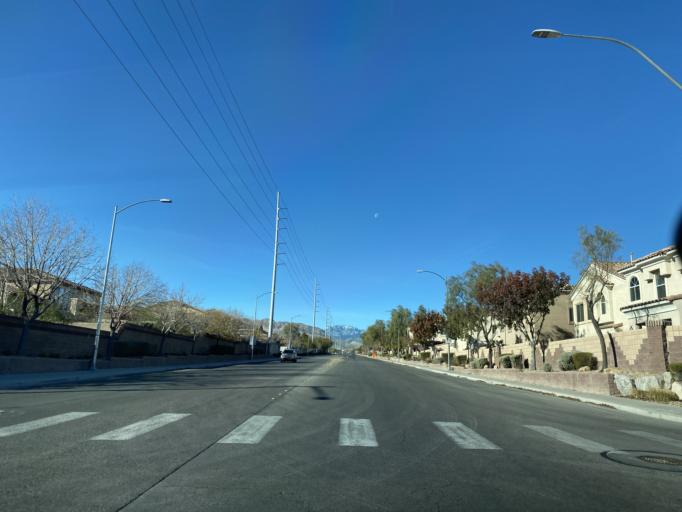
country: US
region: Nevada
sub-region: Clark County
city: Summerlin South
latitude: 36.2993
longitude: -115.3014
